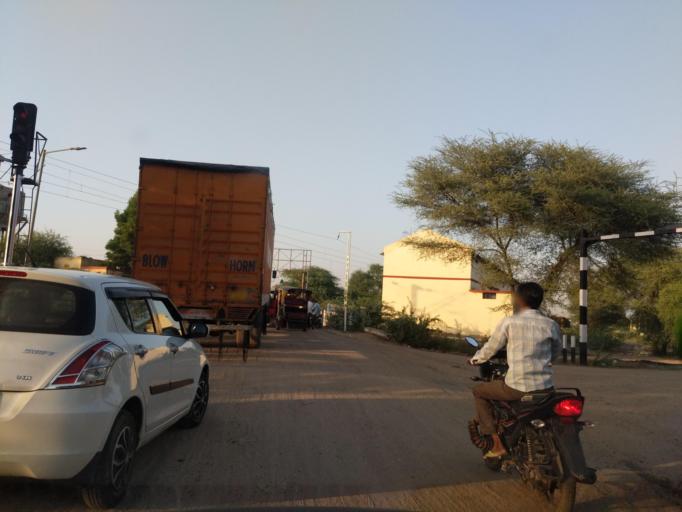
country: IN
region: Rajasthan
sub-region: Churu
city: Rajgarh
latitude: 28.6254
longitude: 75.3801
